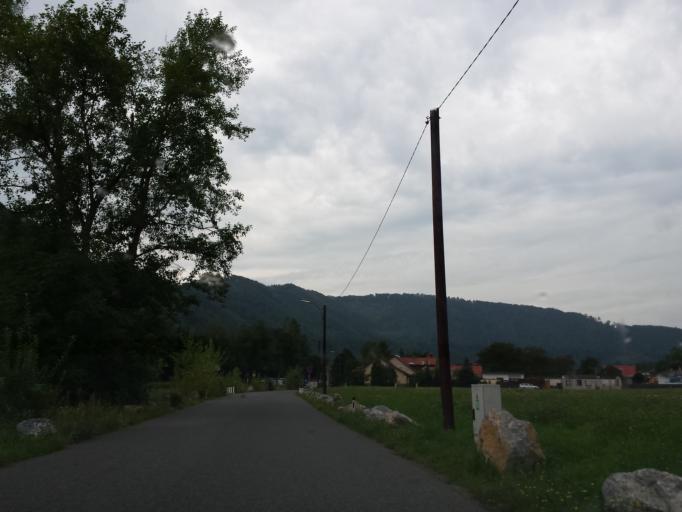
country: AT
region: Styria
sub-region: Graz Stadt
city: Goesting
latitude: 47.1092
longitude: 15.3956
